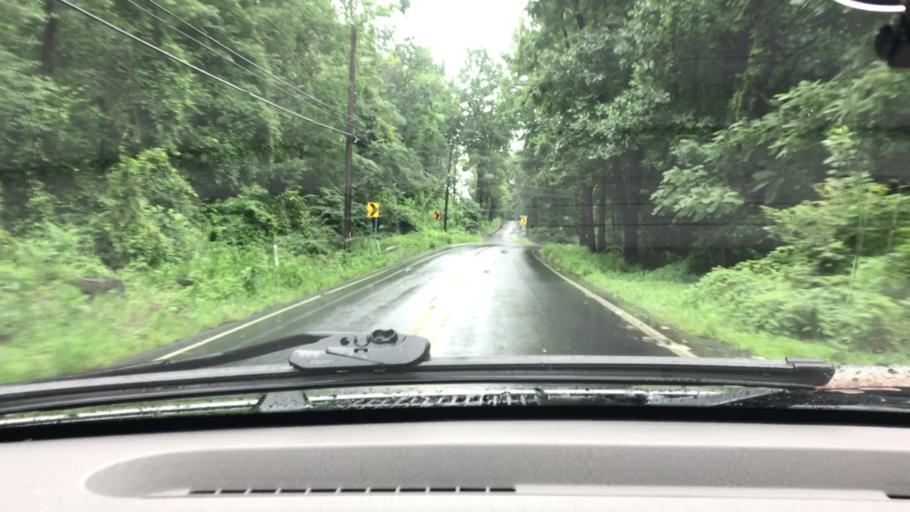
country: US
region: Pennsylvania
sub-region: Lancaster County
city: Elizabethtown
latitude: 40.1819
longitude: -76.5858
